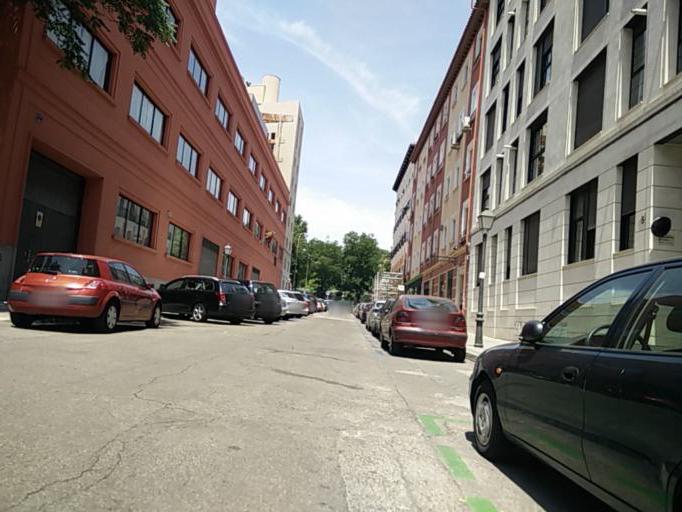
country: ES
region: Madrid
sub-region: Provincia de Madrid
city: Arganzuela
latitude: 40.4046
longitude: -3.7056
